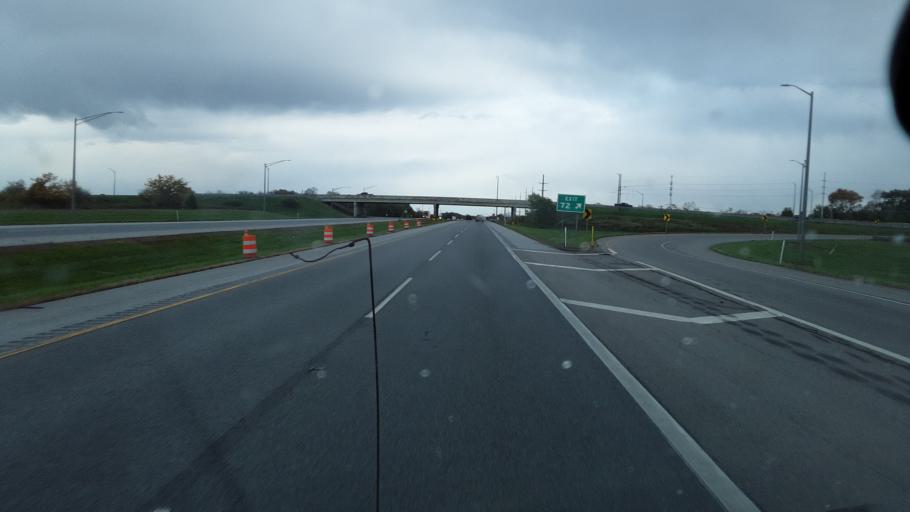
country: US
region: Indiana
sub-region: Saint Joseph County
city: South Bend
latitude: 41.7302
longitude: -86.3366
